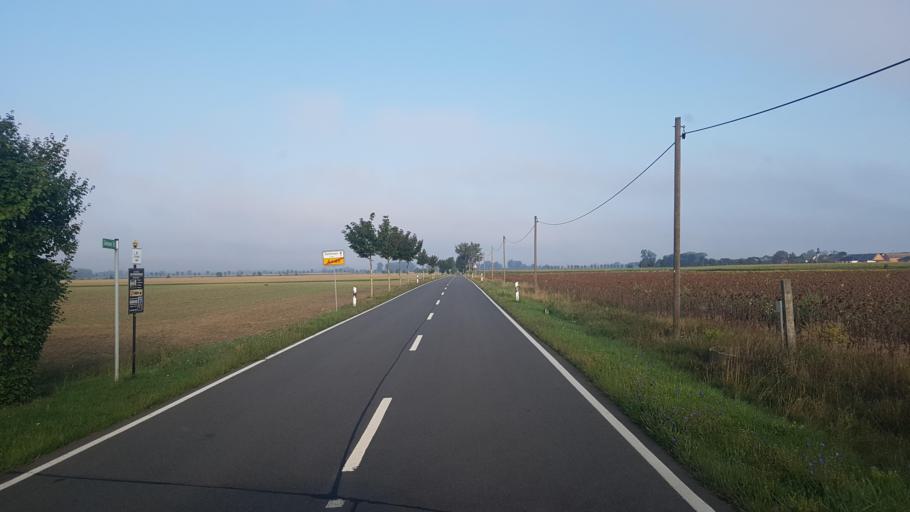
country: DE
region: Saxony-Anhalt
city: Prettin
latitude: 51.7027
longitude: 12.8795
